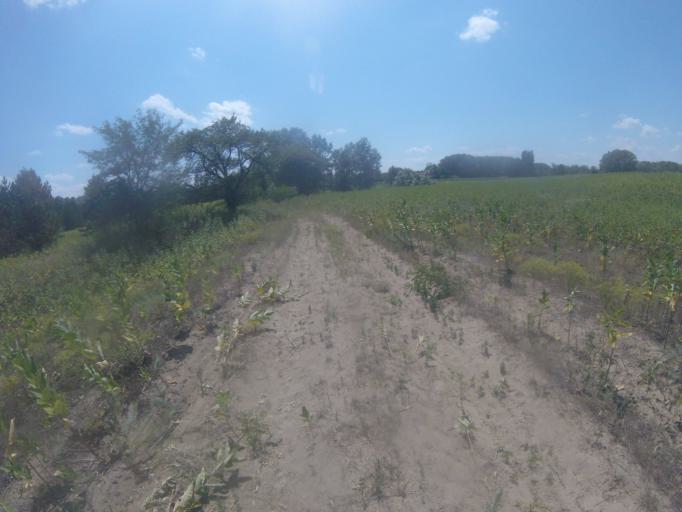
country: HU
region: Bacs-Kiskun
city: Jaszszentlaszlo
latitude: 46.6068
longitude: 19.7139
